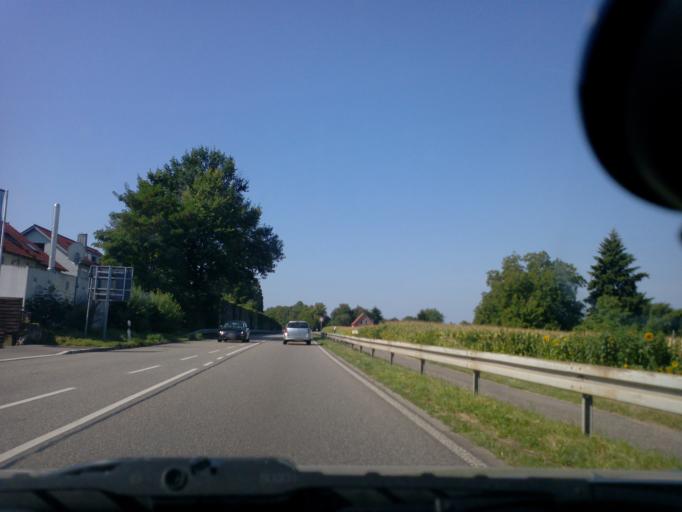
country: DE
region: Baden-Wuerttemberg
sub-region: Karlsruhe Region
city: Weingarten
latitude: 49.0150
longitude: 8.4931
